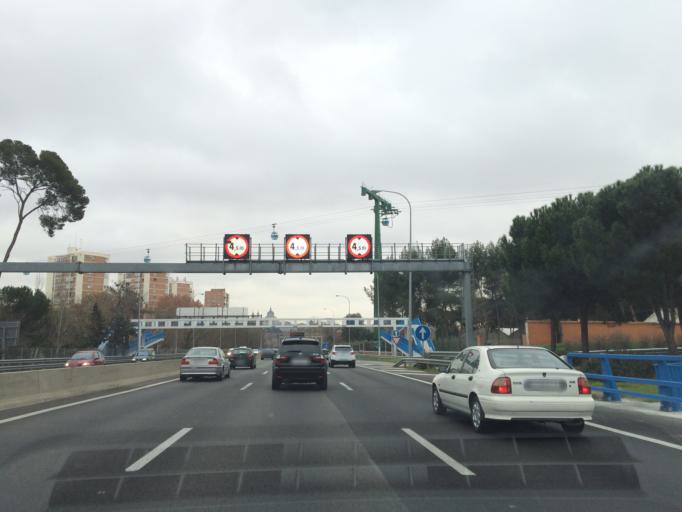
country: ES
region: Madrid
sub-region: Provincia de Madrid
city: Moncloa-Aravaca
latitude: 40.4260
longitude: -3.7330
